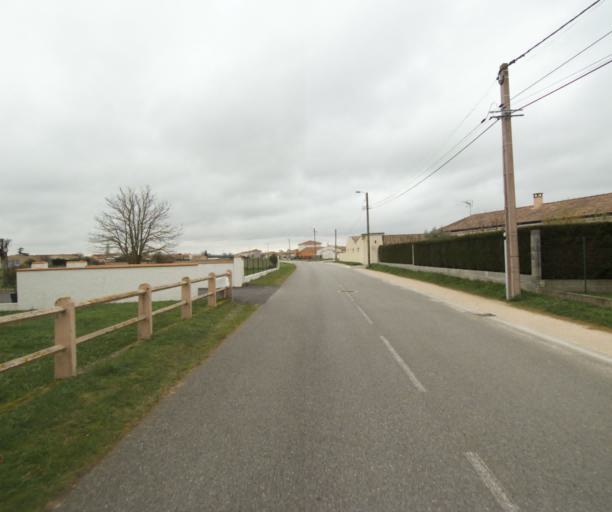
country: FR
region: Midi-Pyrenees
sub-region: Departement de l'Ariege
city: Mazeres
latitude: 43.2452
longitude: 1.6797
